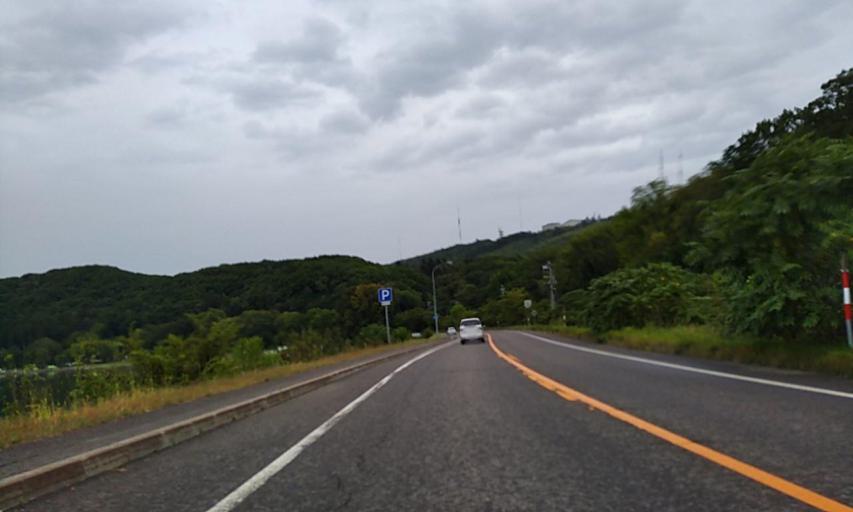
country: JP
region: Hokkaido
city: Abashiri
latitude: 43.9922
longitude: 144.2205
